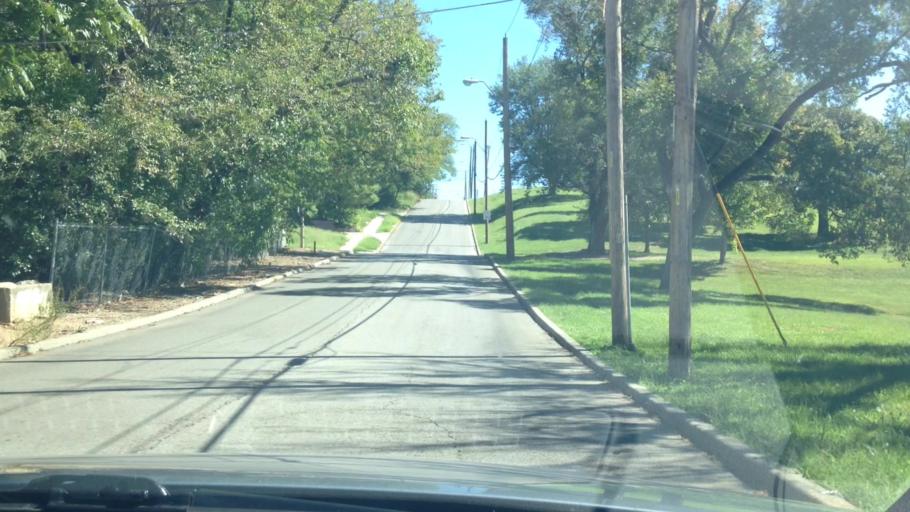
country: US
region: Missouri
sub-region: Jackson County
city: Kansas City
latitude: 39.0484
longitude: -94.5582
